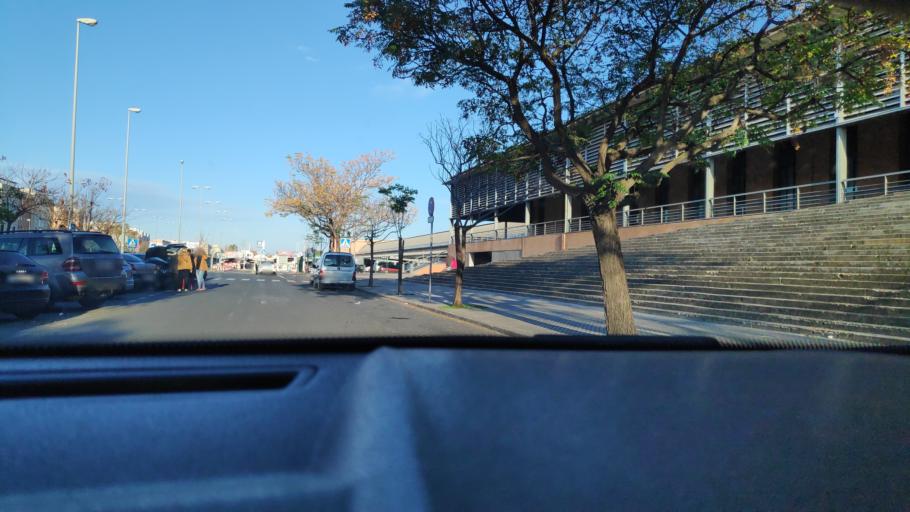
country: ES
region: Andalusia
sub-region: Provincia de Sevilla
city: Sevilla
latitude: 37.3926
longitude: -5.9761
